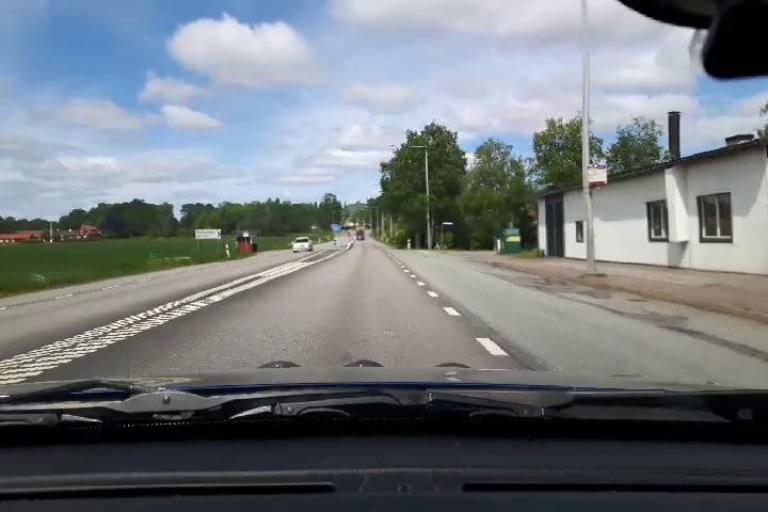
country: SE
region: Uppsala
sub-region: Osthammars Kommun
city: Bjorklinge
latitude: 60.0229
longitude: 17.5544
